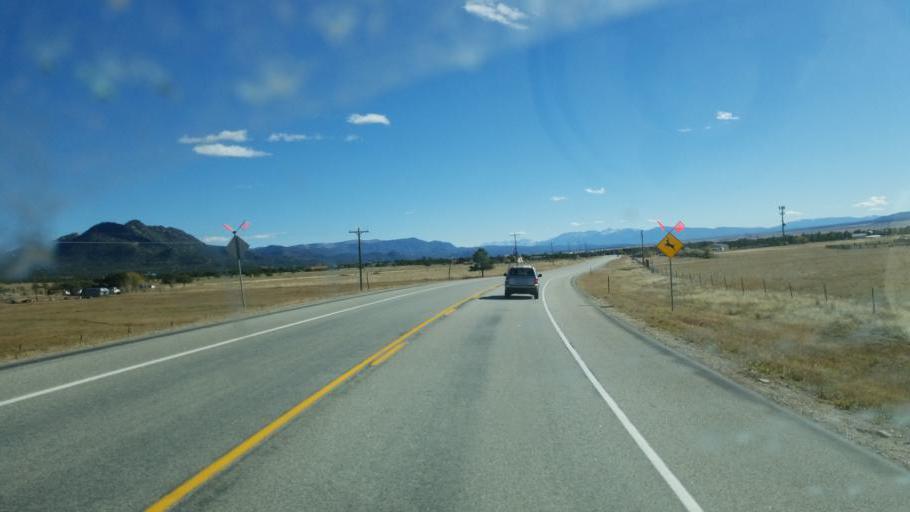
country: US
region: Colorado
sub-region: Chaffee County
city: Buena Vista
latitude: 38.8805
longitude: -106.1616
